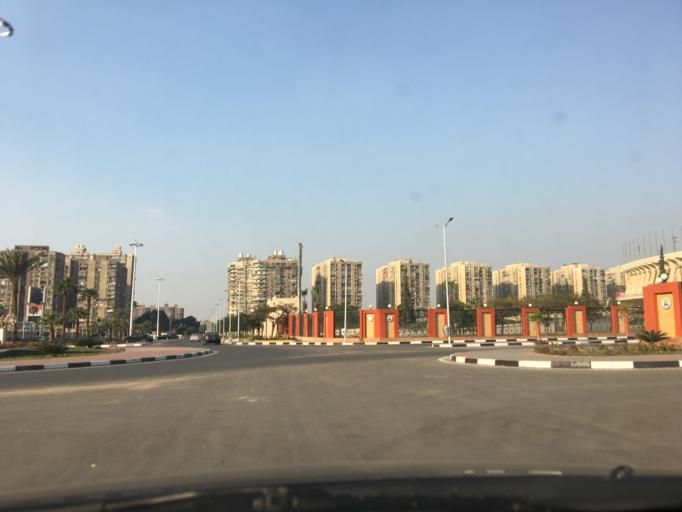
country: EG
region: Muhafazat al Qahirah
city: Cairo
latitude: 30.0733
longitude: 31.3106
